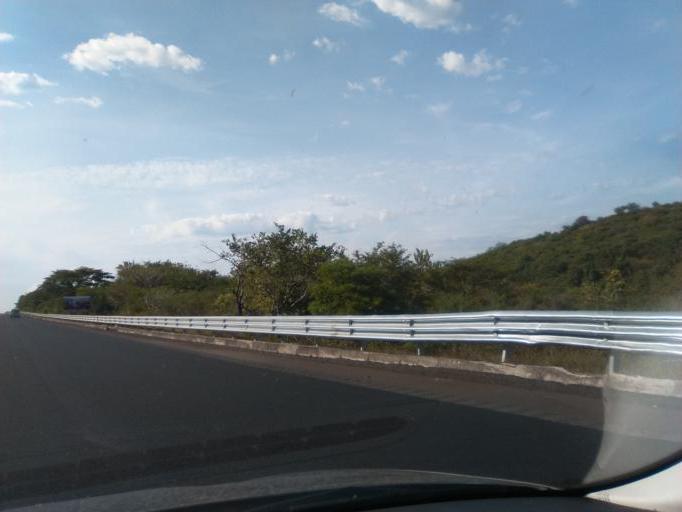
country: MX
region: Morelos
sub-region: Jojutla
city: Higueron
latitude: 18.5653
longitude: -99.2197
